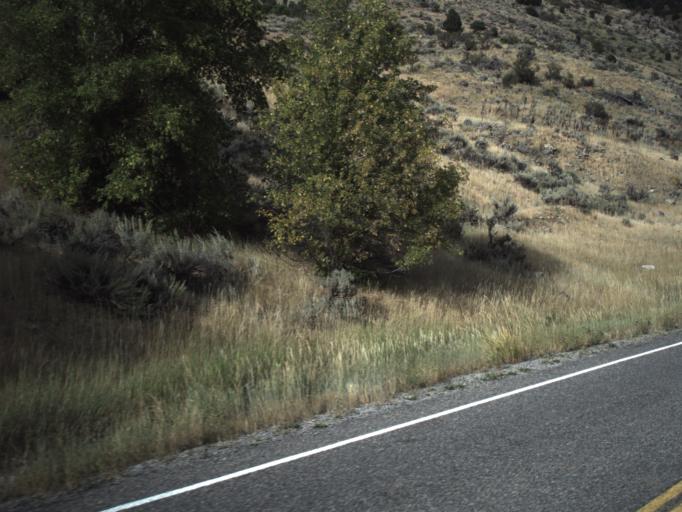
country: US
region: Utah
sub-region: Cache County
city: Millville
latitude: 41.6079
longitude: -111.6190
